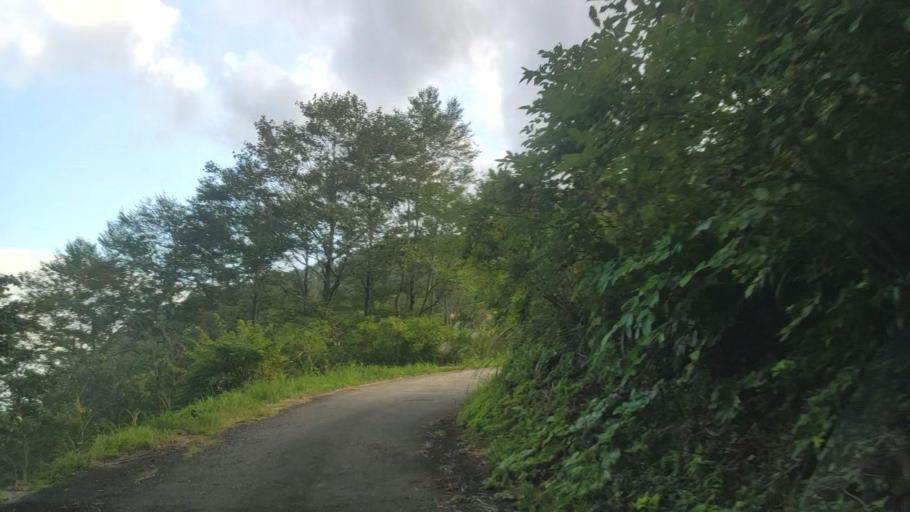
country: JP
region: Toyama
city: Yatsuomachi-higashikumisaka
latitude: 36.3449
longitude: 137.0709
